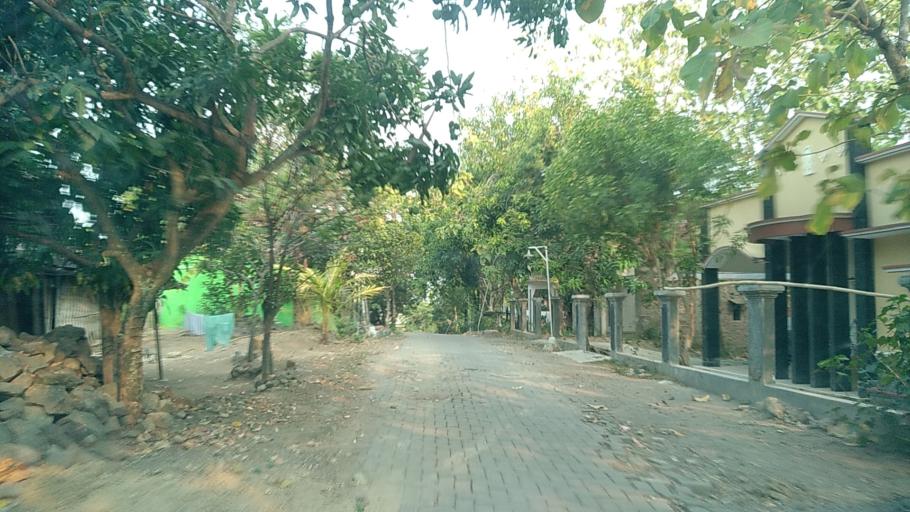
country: ID
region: Central Java
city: Mranggen
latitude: -7.0661
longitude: 110.4832
